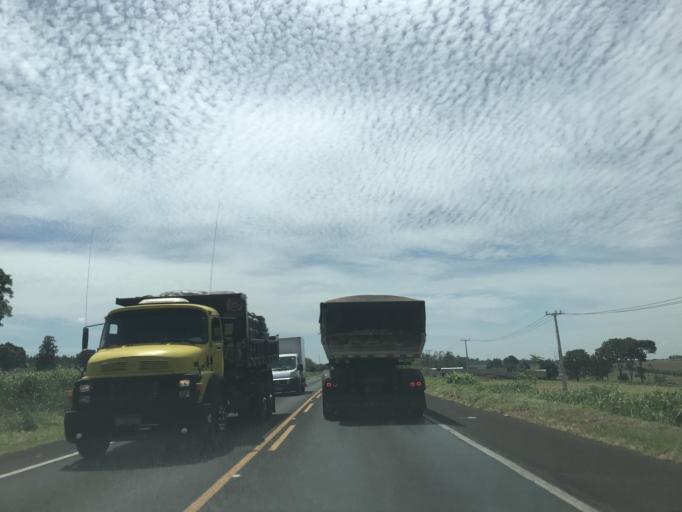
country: BR
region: Parana
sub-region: Paranavai
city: Paranavai
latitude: -23.0153
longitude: -52.5264
